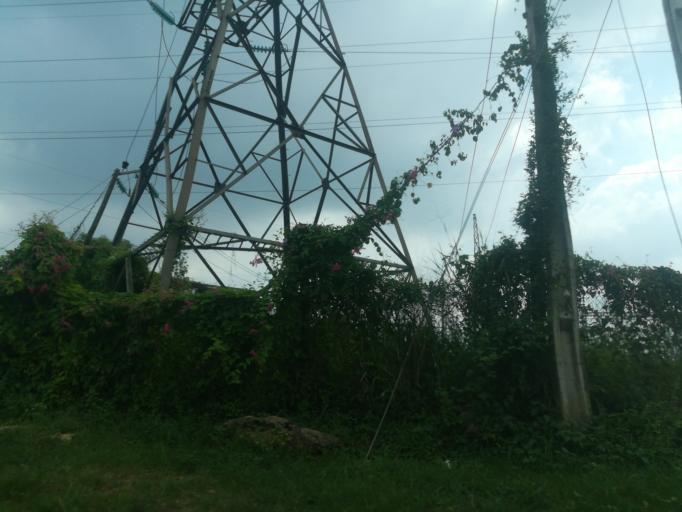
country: NG
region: Oyo
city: Ibadan
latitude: 7.3739
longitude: 3.8569
